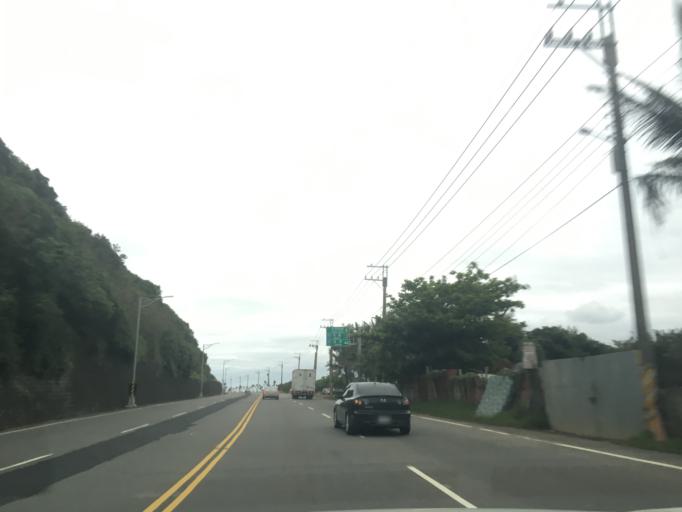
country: TW
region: Taiwan
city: Hengchun
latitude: 22.3430
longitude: 120.8970
